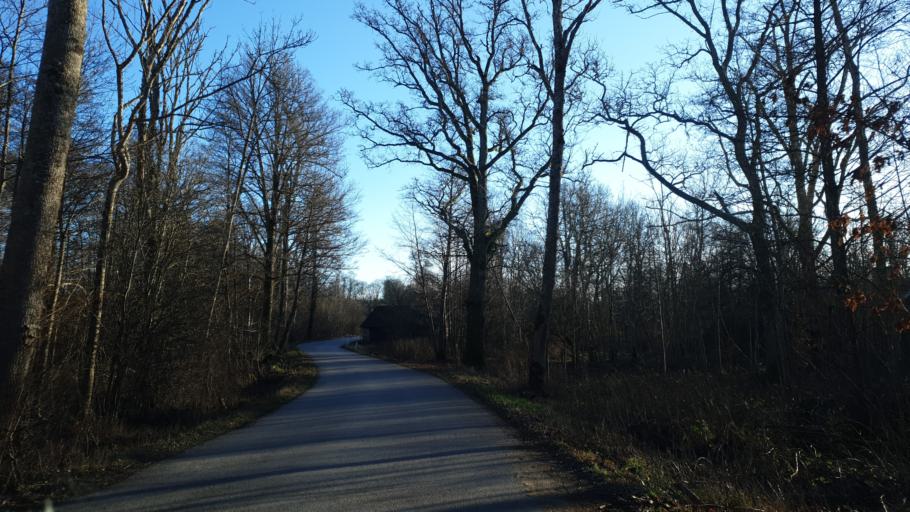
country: SE
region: Blekinge
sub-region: Karlskrona Kommun
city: Nattraby
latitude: 56.2462
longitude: 15.4166
